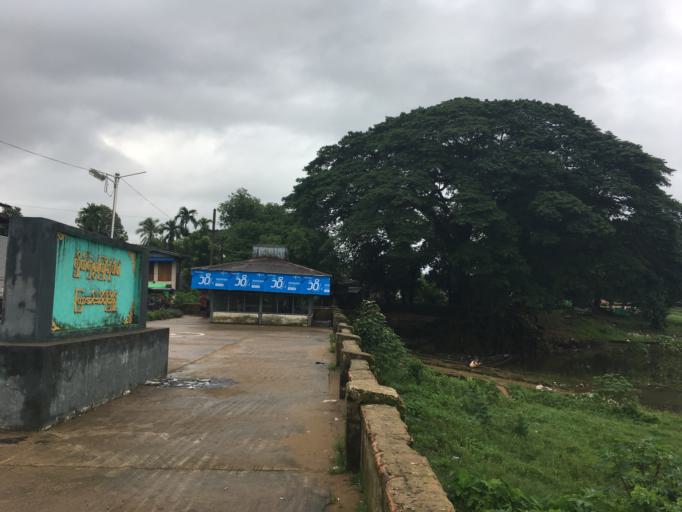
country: MM
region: Mon
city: Mudon
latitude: 16.0377
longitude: 98.1180
